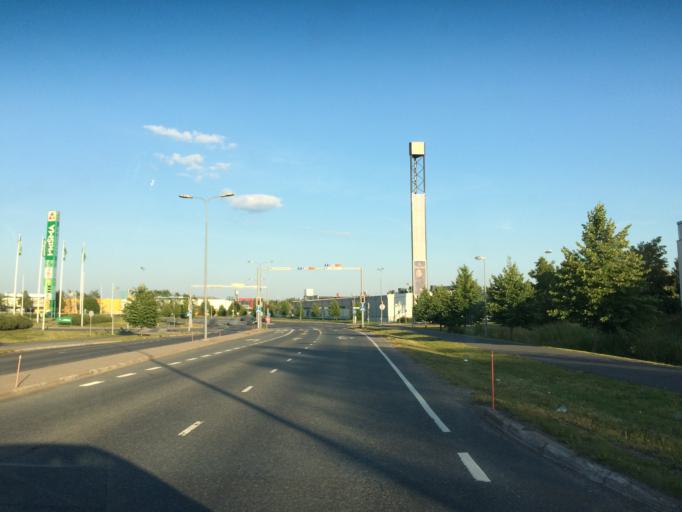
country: FI
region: Haeme
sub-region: Haemeenlinna
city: Haemeenlinna
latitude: 61.0106
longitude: 24.4119
